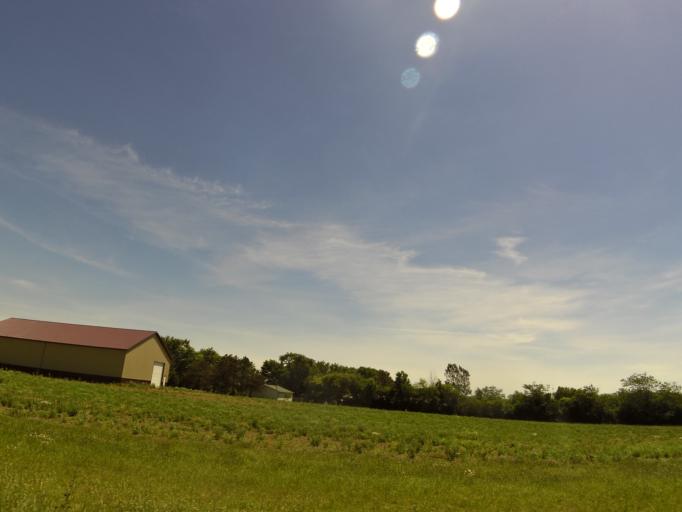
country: US
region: Illinois
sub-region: Vermilion County
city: Rossville
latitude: 40.2717
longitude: -87.6535
